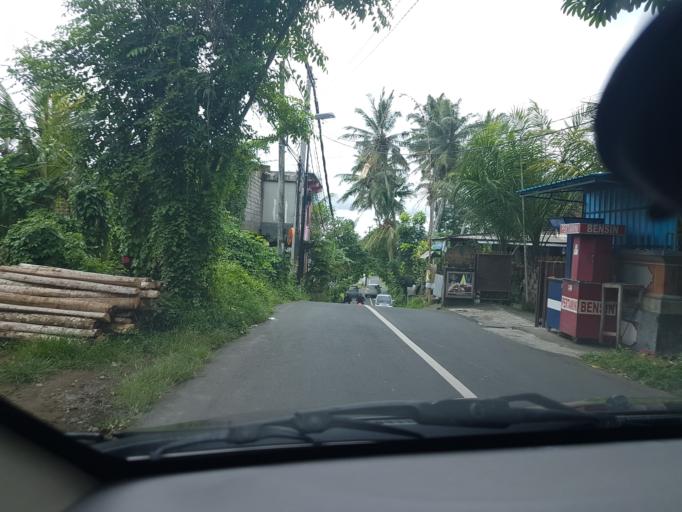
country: ID
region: Bali
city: Banjar Triwangsakeliki
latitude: -8.4673
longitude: 115.2718
